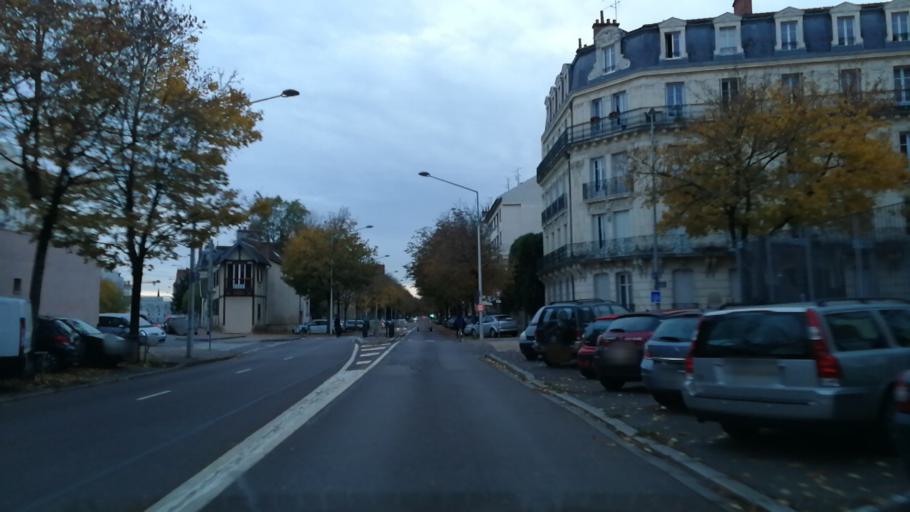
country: FR
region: Bourgogne
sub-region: Departement de la Cote-d'Or
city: Dijon
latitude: 47.3209
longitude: 5.0509
